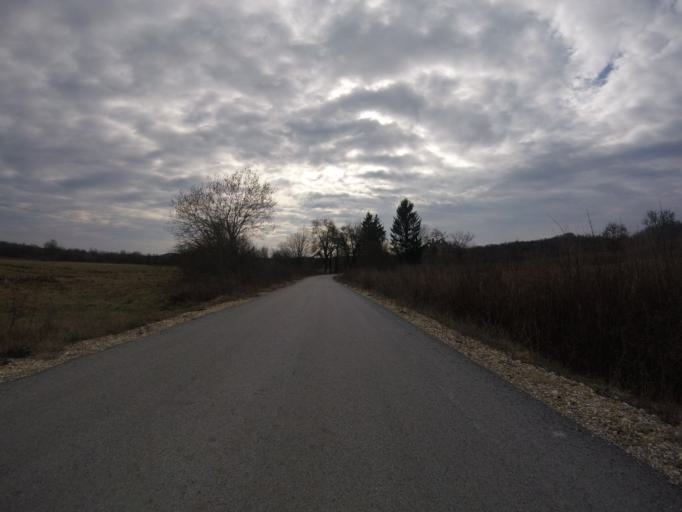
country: HR
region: Sisacko-Moslavacka
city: Glina
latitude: 45.4411
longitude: 16.0738
